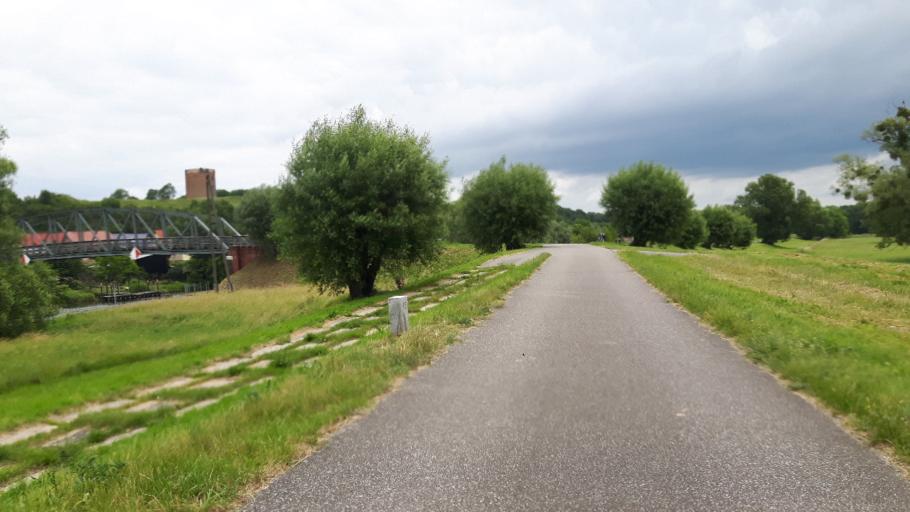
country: DE
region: Brandenburg
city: Schoneberg
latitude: 52.9763
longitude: 14.1145
